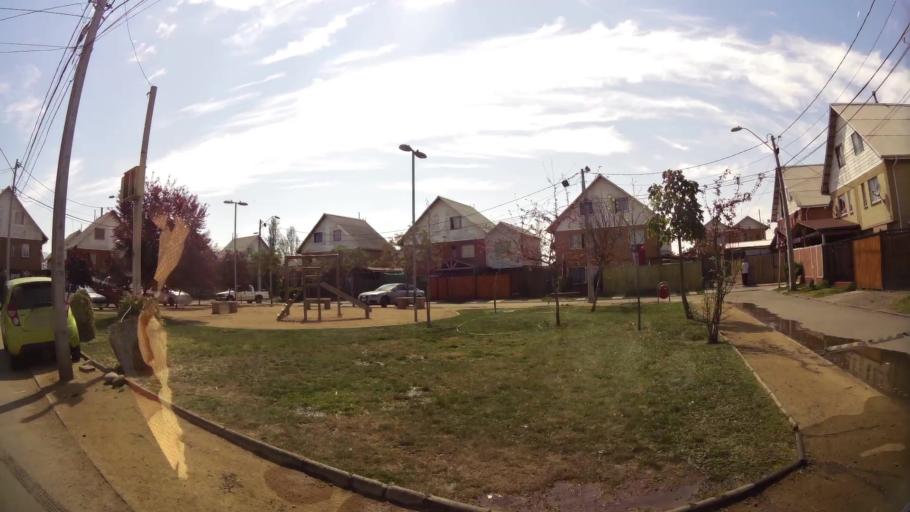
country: CL
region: Santiago Metropolitan
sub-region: Provincia de Talagante
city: Talagante
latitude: -33.6622
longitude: -70.9155
